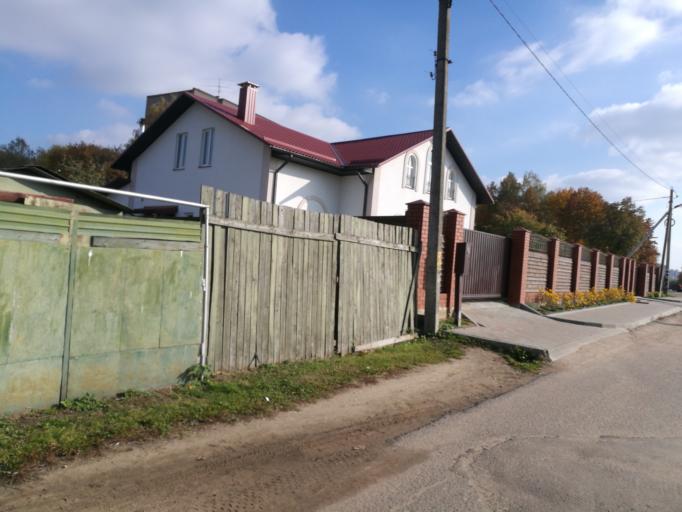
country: BY
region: Minsk
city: Minsk
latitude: 53.8989
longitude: 27.5176
